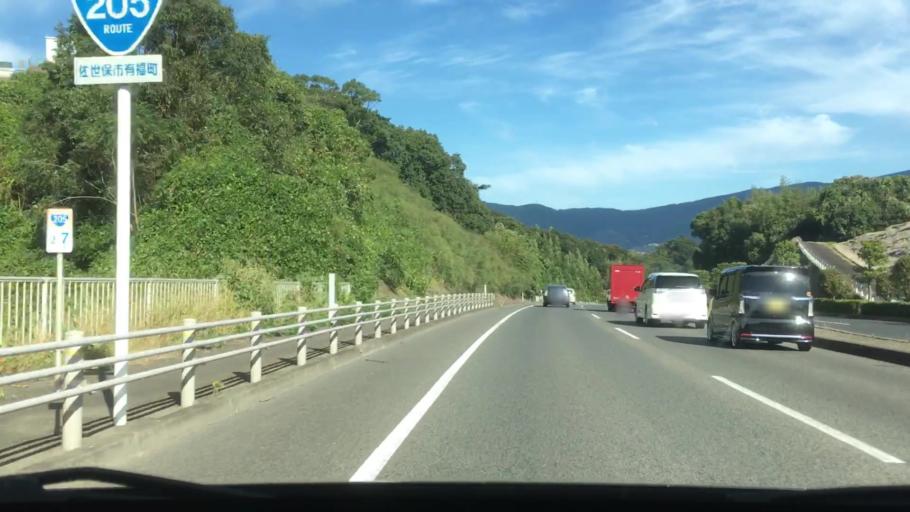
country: JP
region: Nagasaki
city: Sasebo
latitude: 33.1291
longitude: 129.7874
